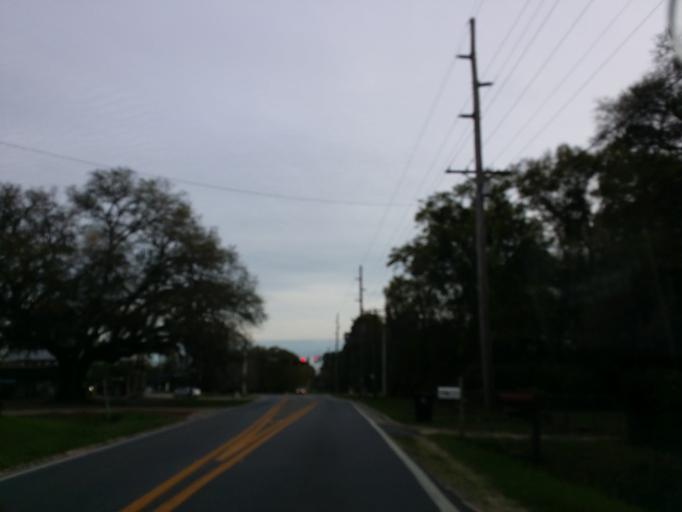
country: US
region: Florida
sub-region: Leon County
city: Tallahassee
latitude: 30.4926
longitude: -84.1255
